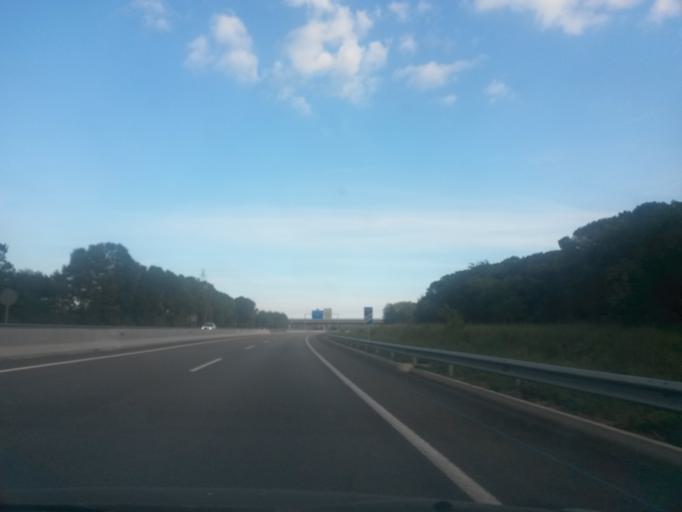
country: ES
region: Catalonia
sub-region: Provincia de Girona
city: Vilobi d'Onyar
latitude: 41.8753
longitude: 2.7539
